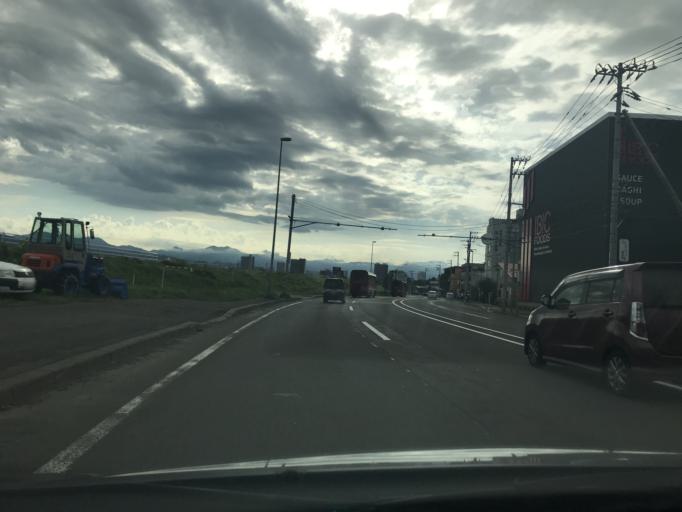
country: JP
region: Hokkaido
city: Sapporo
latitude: 43.0703
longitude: 141.3952
